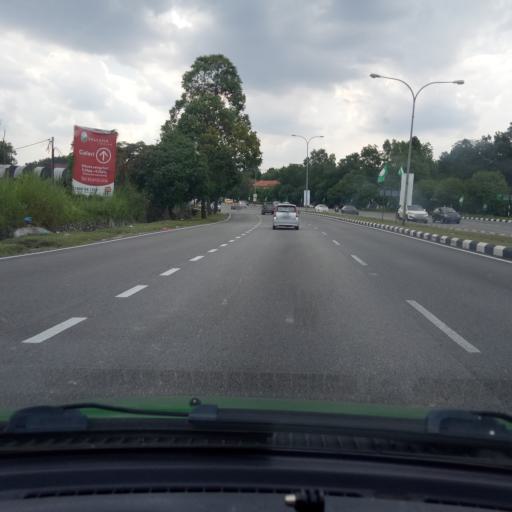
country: MY
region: Selangor
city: Kampong Baharu Balakong
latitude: 3.0114
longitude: 101.7983
